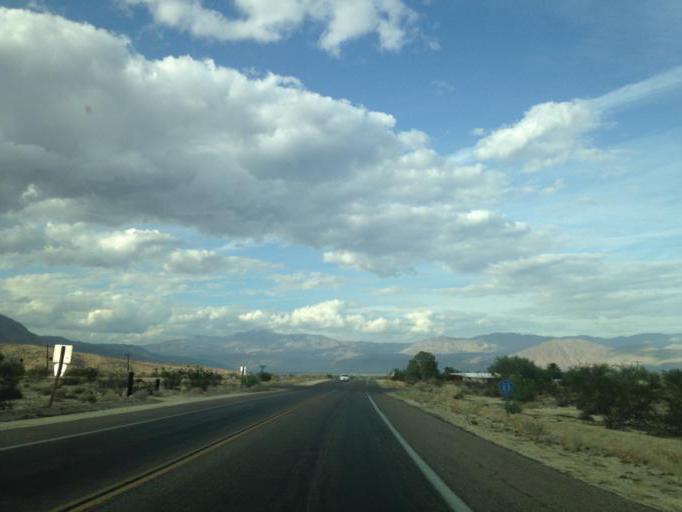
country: US
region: California
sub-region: San Diego County
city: Borrego Springs
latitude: 33.2305
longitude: -116.3759
